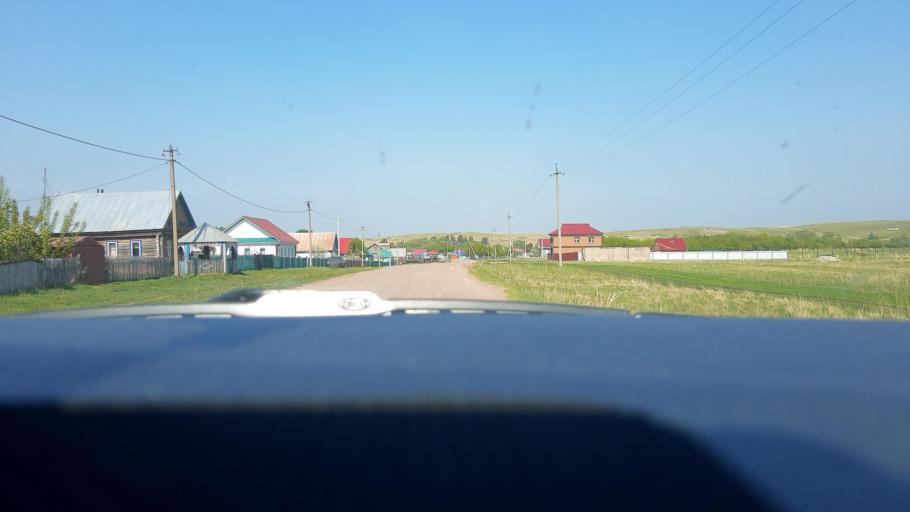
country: RU
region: Bashkortostan
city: Chishmy
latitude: 54.4498
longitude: 55.3213
